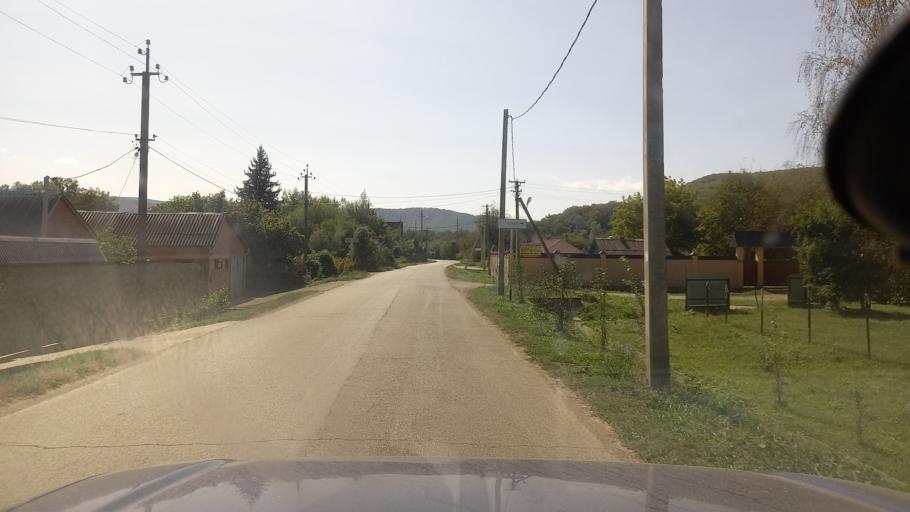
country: RU
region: Krasnodarskiy
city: Azovskaya
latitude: 44.7078
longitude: 38.6727
